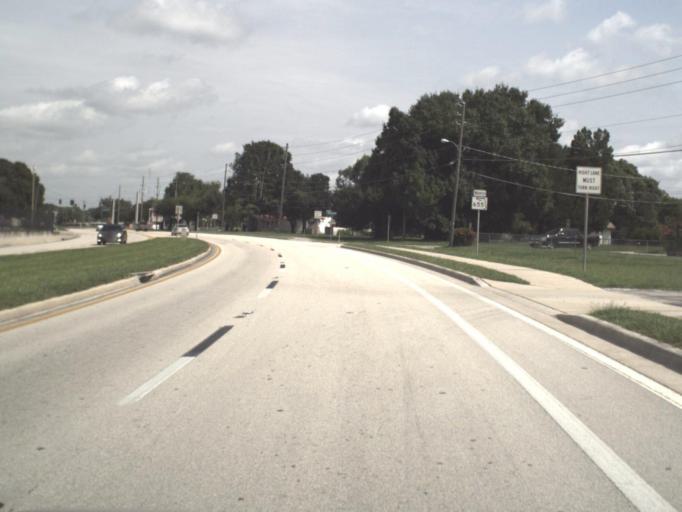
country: US
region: Florida
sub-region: Polk County
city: Jan-Phyl Village
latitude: 28.0054
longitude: -81.7516
